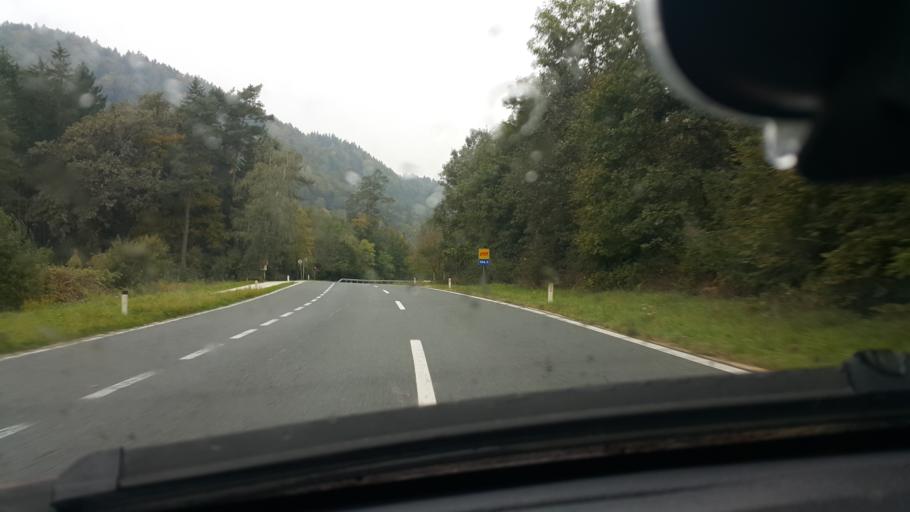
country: SI
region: Dravograd
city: Dravograd
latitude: 46.6078
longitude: 14.9793
